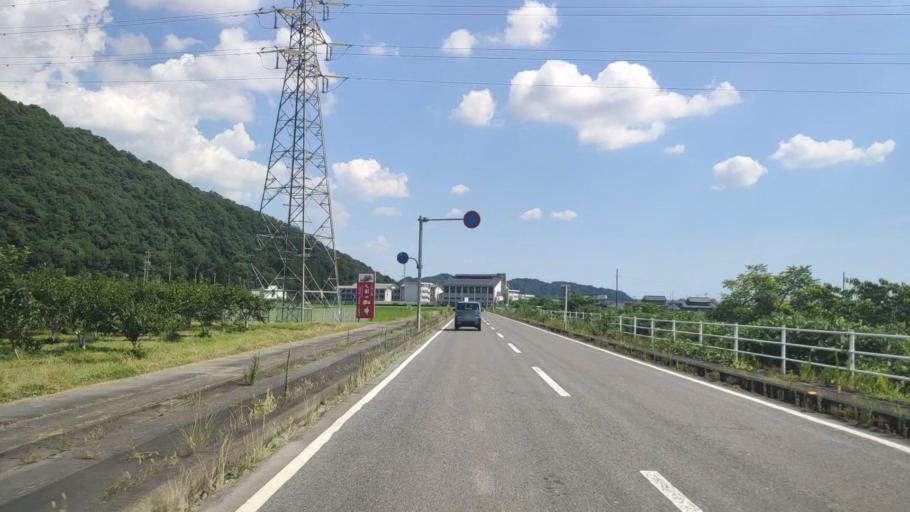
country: JP
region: Gifu
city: Godo
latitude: 35.4938
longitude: 136.6717
